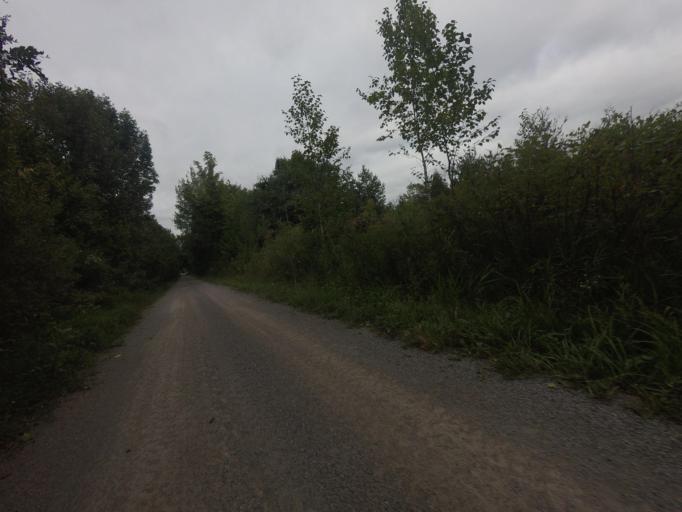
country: CA
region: Ontario
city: Omemee
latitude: 44.4664
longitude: -78.7543
